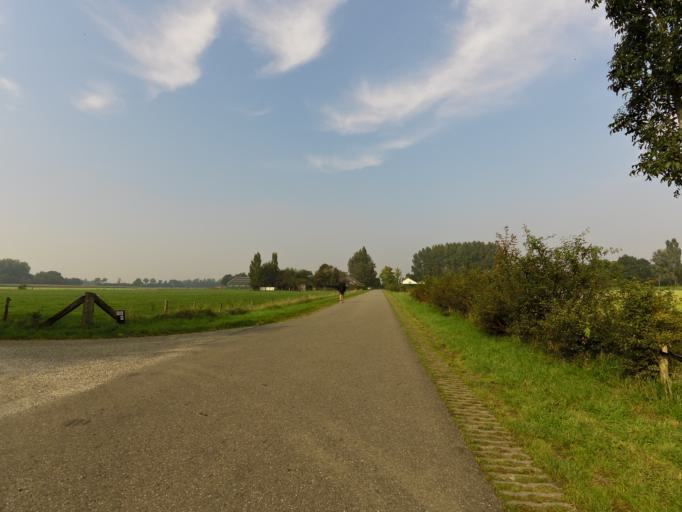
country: NL
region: Gelderland
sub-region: Gemeente Doetinchem
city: Doetinchem
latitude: 51.9462
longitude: 6.2572
